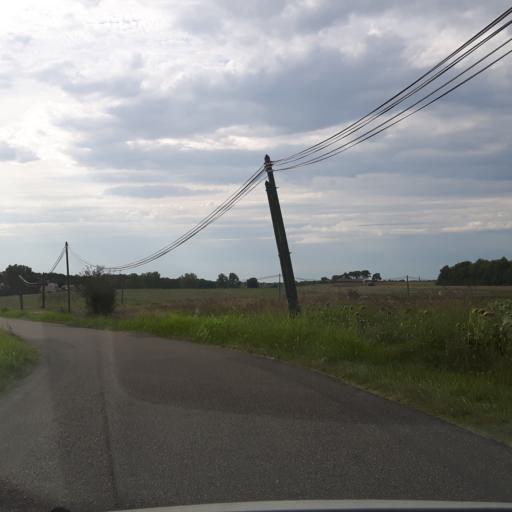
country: FR
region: Midi-Pyrenees
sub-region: Departement de la Haute-Garonne
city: Castelnau-d'Estretefonds
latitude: 43.7981
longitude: 1.3556
